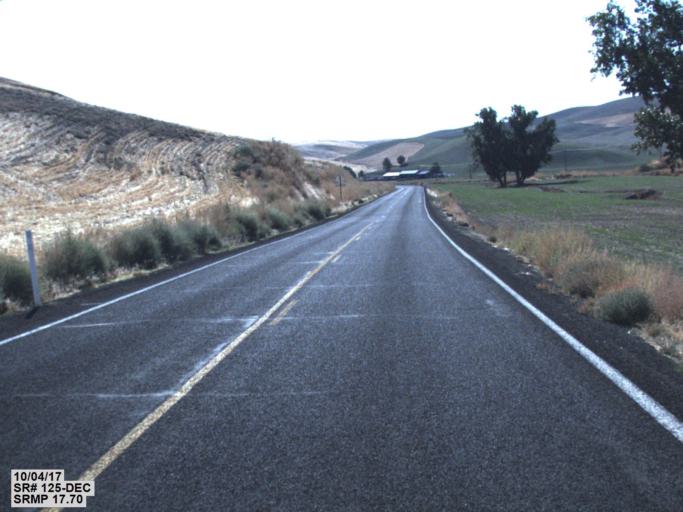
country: US
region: Washington
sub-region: Walla Walla County
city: Walla Walla
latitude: 46.2222
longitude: -118.3892
